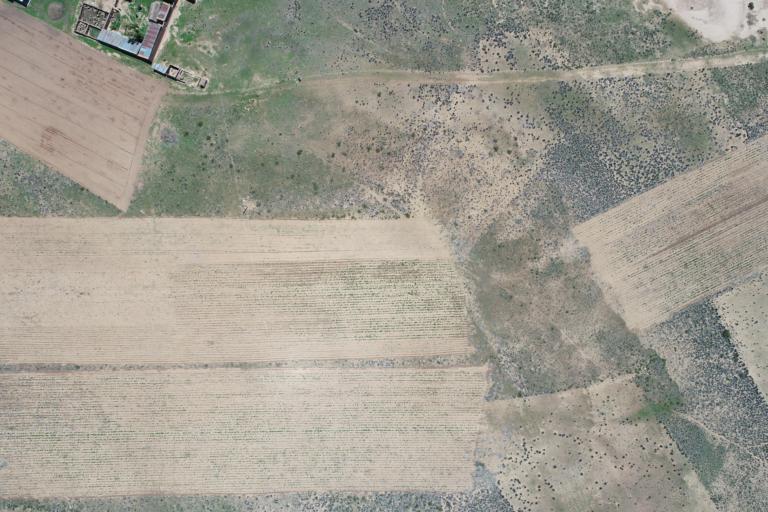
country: BO
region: La Paz
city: Curahuara de Carangas
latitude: -17.3102
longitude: -68.5084
